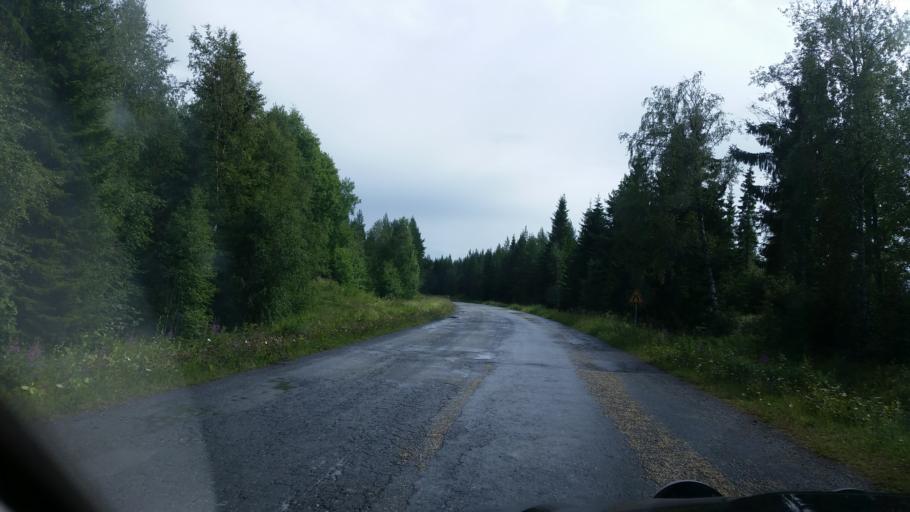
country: SE
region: Jaemtland
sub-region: Krokoms Kommun
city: Krokom
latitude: 63.3214
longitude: 14.3039
